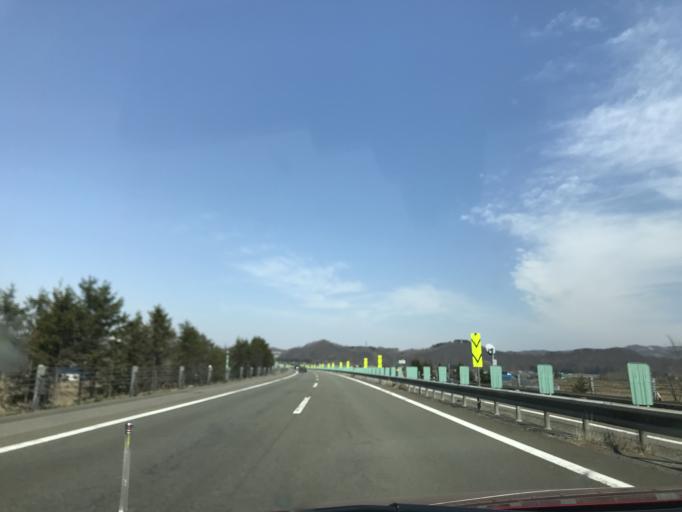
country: JP
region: Hokkaido
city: Iwamizawa
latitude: 43.2265
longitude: 141.8302
